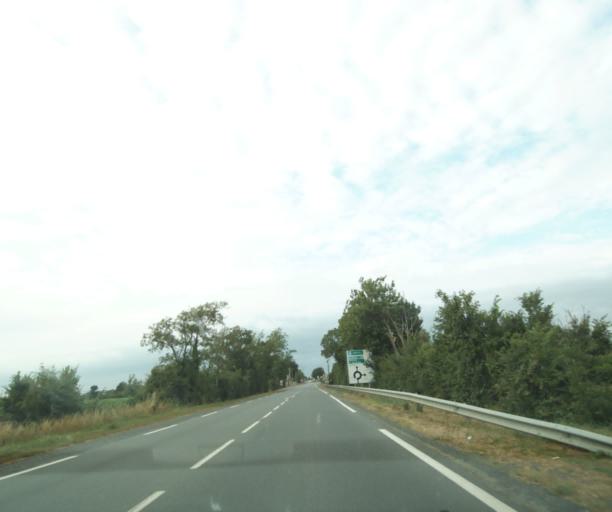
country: FR
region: Poitou-Charentes
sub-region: Departement de la Charente-Maritime
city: Marans
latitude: 46.2935
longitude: -0.9918
